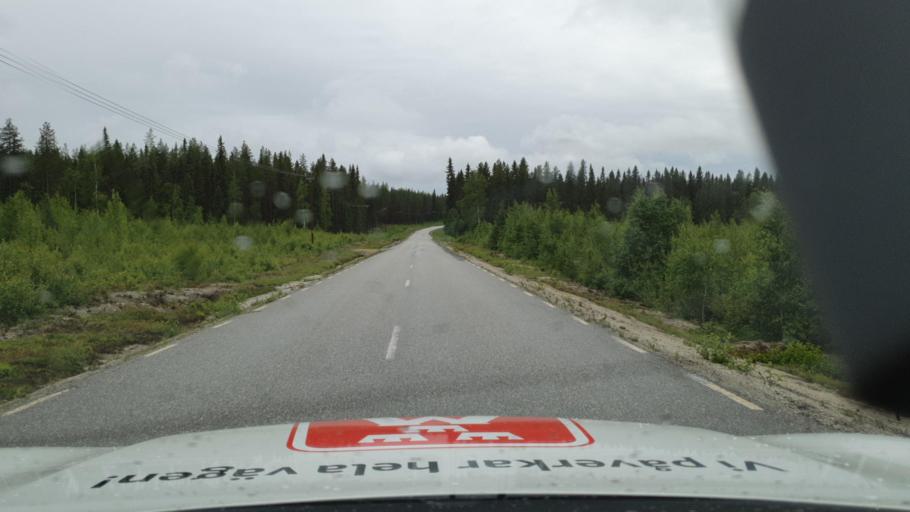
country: SE
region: Vaesterbotten
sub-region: Asele Kommun
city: Asele
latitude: 63.9910
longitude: 17.1690
